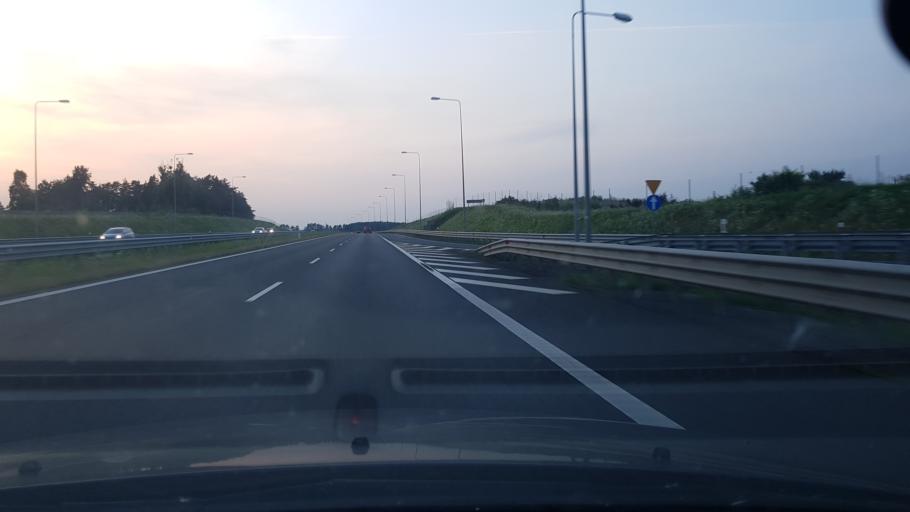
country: PL
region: Warmian-Masurian Voivodeship
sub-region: Powiat olsztynski
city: Olsztynek
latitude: 53.5016
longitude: 20.3117
